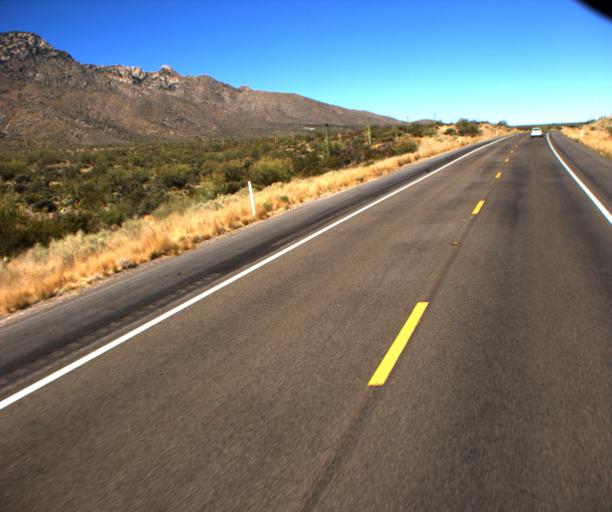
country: US
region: Arizona
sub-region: Pima County
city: Three Points
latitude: 32.0379
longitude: -111.5089
